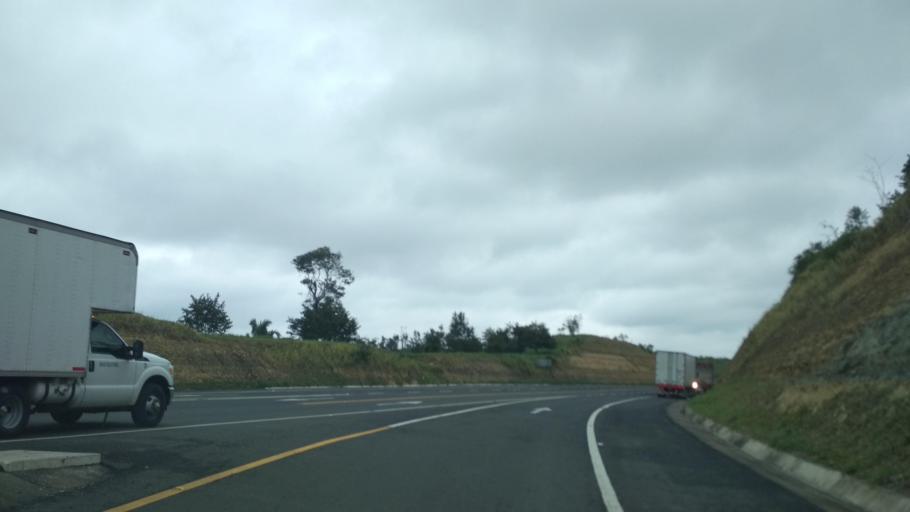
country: MX
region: Veracruz
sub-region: Papantla
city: Polutla
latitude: 20.4587
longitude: -97.2457
